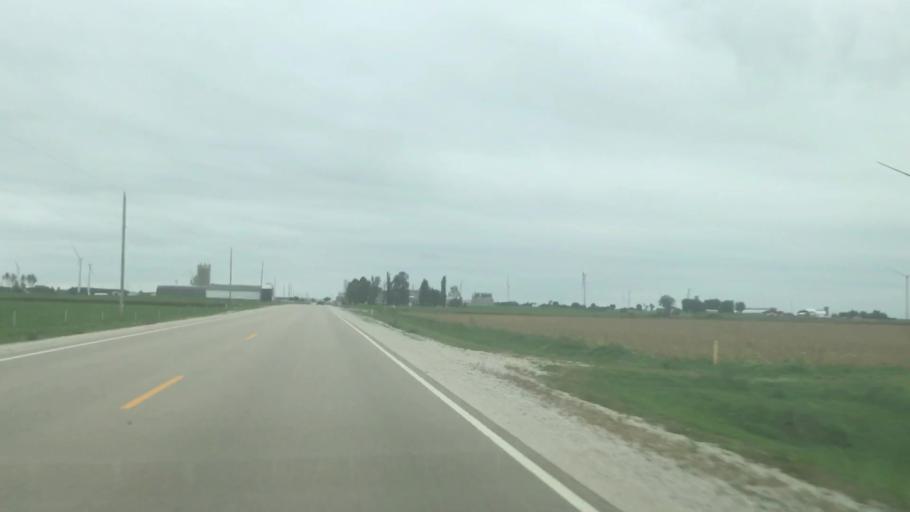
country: US
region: Wisconsin
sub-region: Fond du Lac County
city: Oakfield
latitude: 43.6252
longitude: -88.5418
